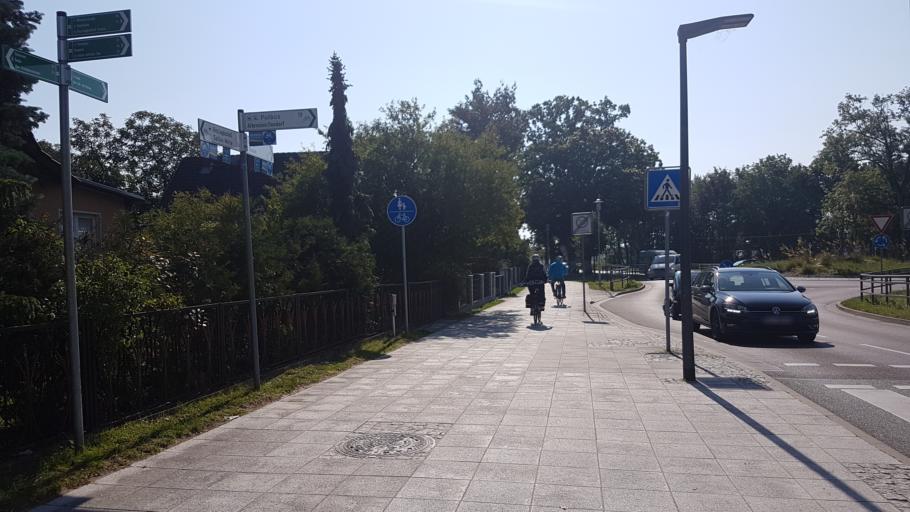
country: DE
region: Mecklenburg-Vorpommern
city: Ostseebad Sellin
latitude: 54.3718
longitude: 13.7000
